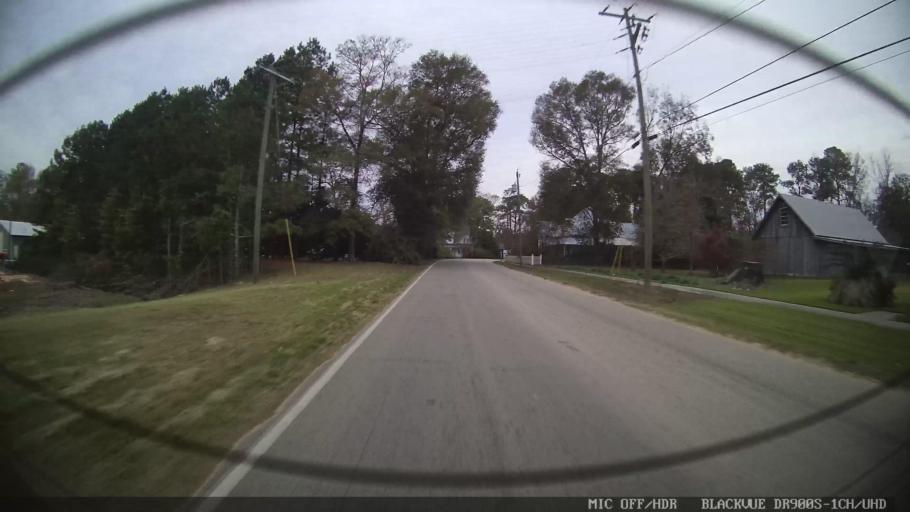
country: US
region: Mississippi
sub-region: Clarke County
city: Stonewall
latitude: 32.0406
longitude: -88.8861
